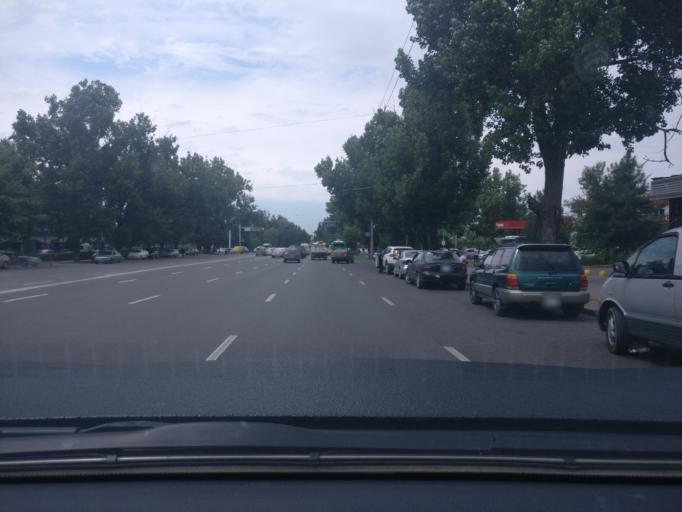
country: KZ
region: Almaty Qalasy
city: Almaty
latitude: 43.2444
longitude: 76.8568
